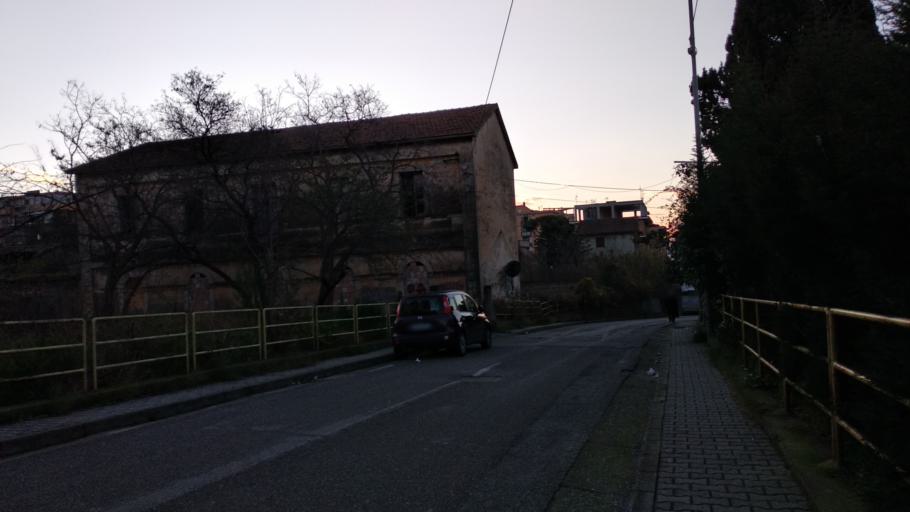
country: IT
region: Calabria
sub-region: Provincia di Catanzaro
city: Barone
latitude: 38.8290
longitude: 16.6250
